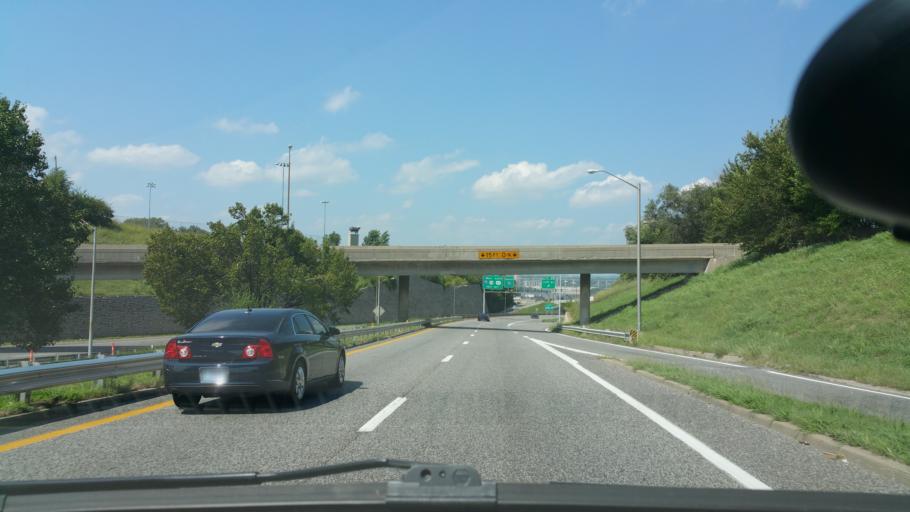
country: US
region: Missouri
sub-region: Jackson County
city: Kansas City
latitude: 39.0976
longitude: -94.5917
